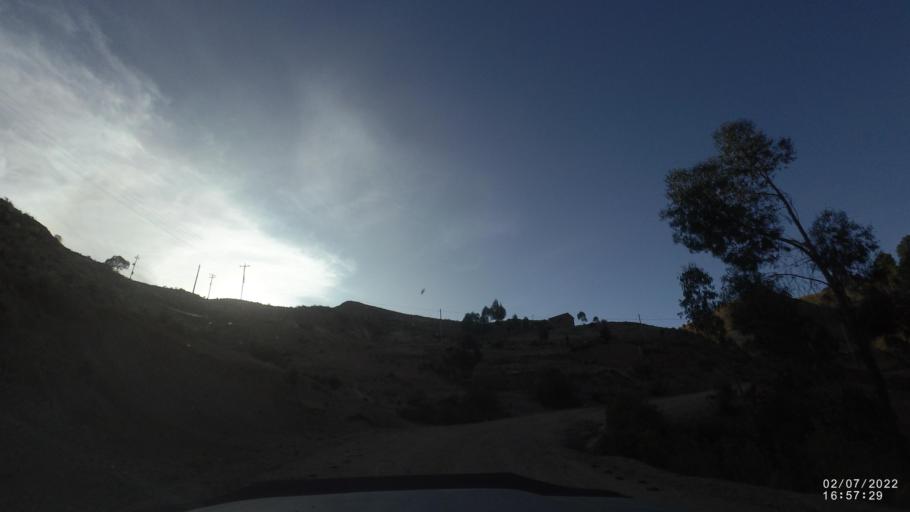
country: BO
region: Cochabamba
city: Irpa Irpa
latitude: -17.9486
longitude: -66.5461
